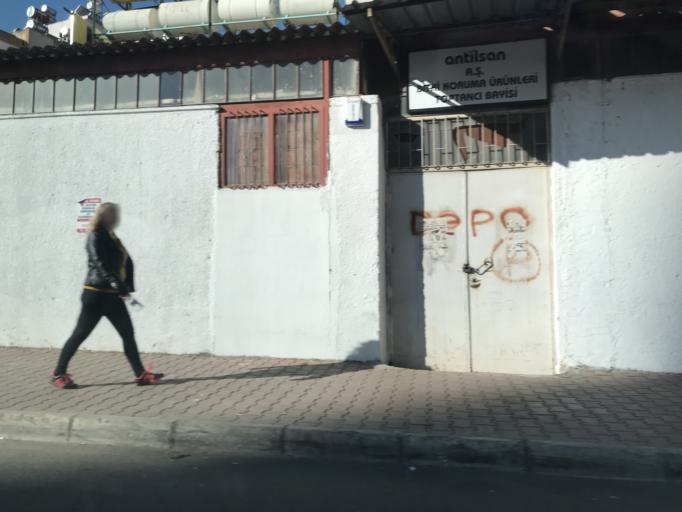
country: TR
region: Antalya
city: Antalya
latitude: 36.8983
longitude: 30.7074
